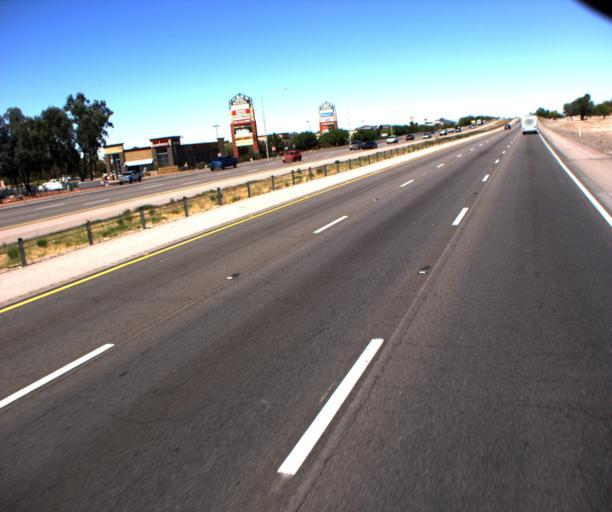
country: US
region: Arizona
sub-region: Pima County
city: Tortolita
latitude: 32.3542
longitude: -111.0848
